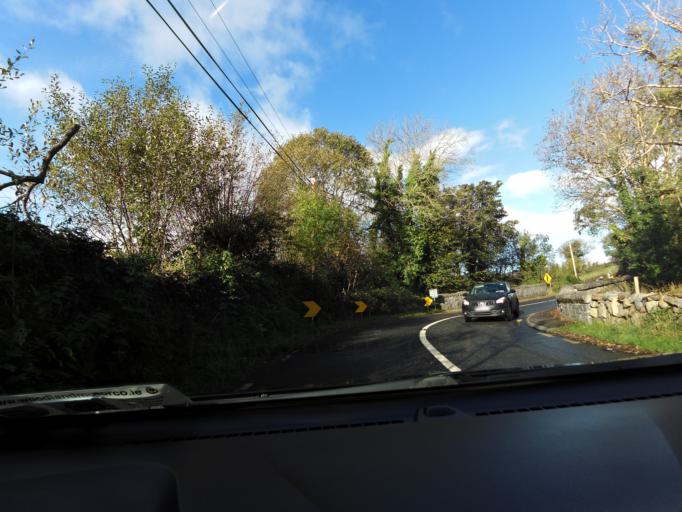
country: IE
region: Connaught
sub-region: Maigh Eo
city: Westport
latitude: 53.8124
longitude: -9.5344
